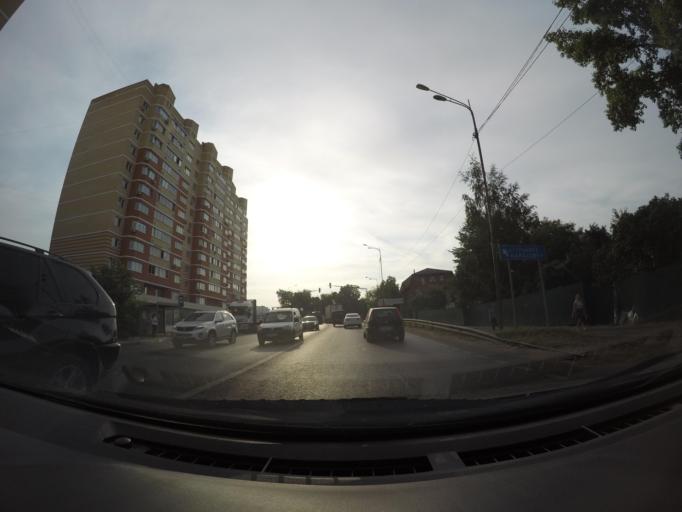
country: RU
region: Moskovskaya
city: Kraskovo
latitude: 55.6577
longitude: 37.9834
